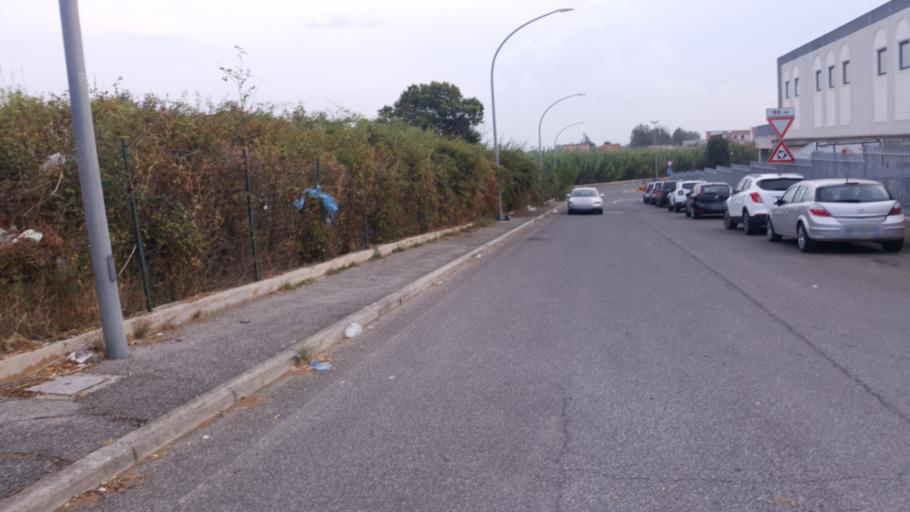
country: IT
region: Latium
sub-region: Citta metropolitana di Roma Capitale
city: Colonna
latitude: 41.8182
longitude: 12.7682
